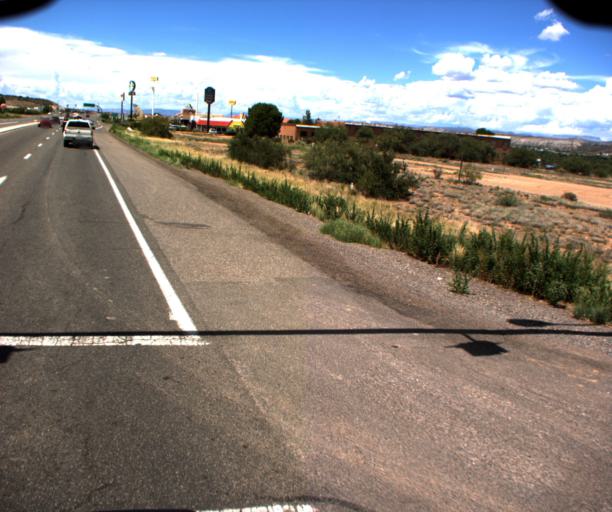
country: US
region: Arizona
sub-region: Yavapai County
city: Camp Verde
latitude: 34.5726
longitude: -111.8807
